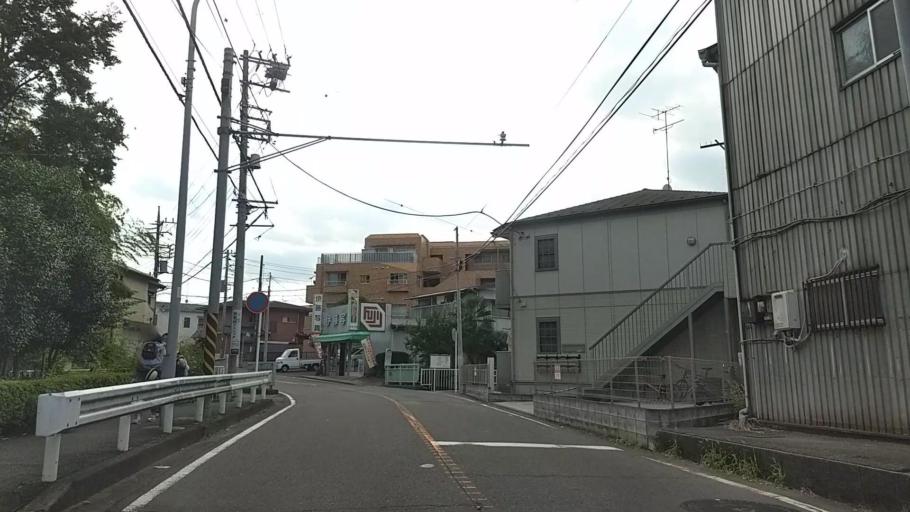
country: JP
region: Kanagawa
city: Yokohama
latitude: 35.5005
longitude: 139.5834
